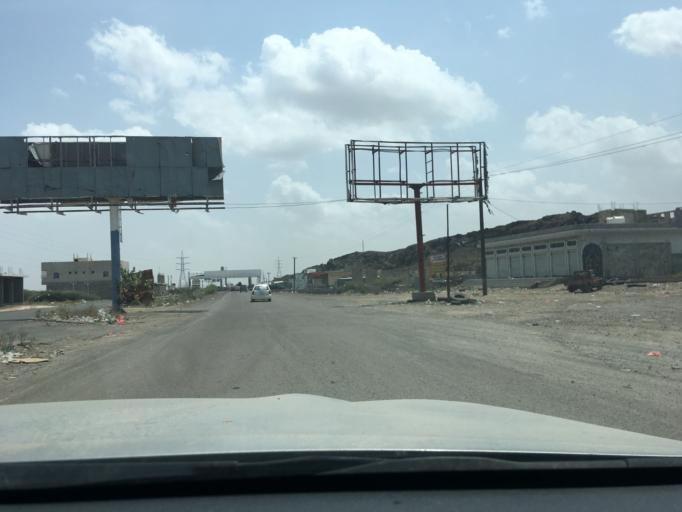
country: YE
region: Lahij
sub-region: Al Milah
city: Al Milah
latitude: 13.2876
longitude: 44.7563
